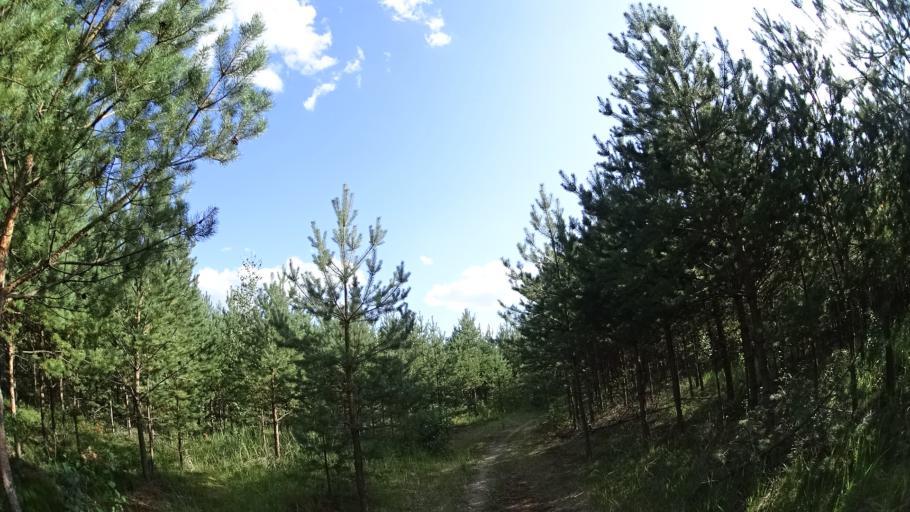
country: FI
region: Uusimaa
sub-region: Helsinki
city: Vihti
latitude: 60.3693
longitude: 24.3659
